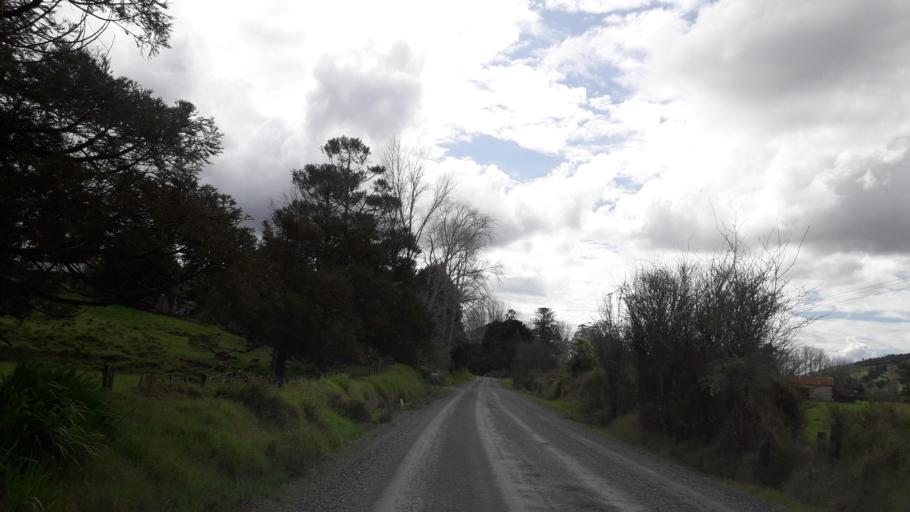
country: NZ
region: Northland
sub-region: Far North District
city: Taipa
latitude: -35.0882
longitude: 173.5124
